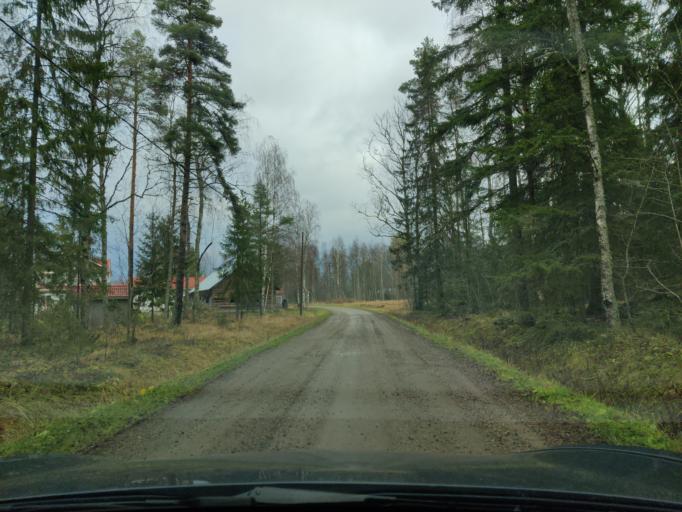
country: FI
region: Northern Savo
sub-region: Ylae-Savo
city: Kiuruvesi
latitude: 63.6390
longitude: 26.6545
